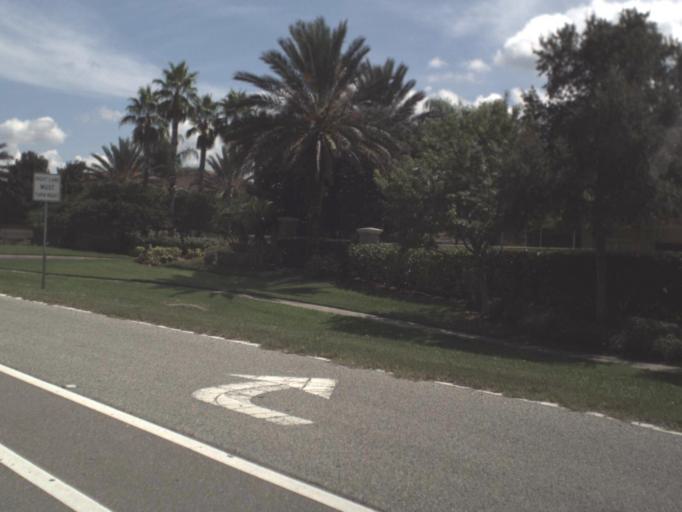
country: US
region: Florida
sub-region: Sarasota County
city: Desoto Lakes
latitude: 27.3883
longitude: -82.5004
